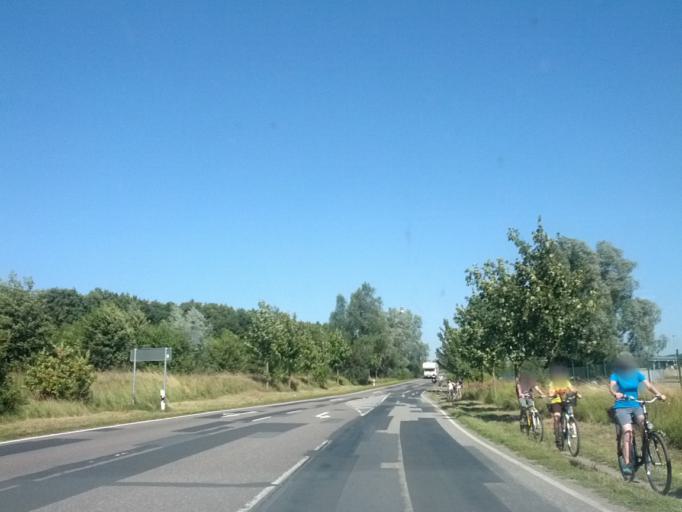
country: DE
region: Mecklenburg-Vorpommern
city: Sagard
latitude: 54.4842
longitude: 13.5777
